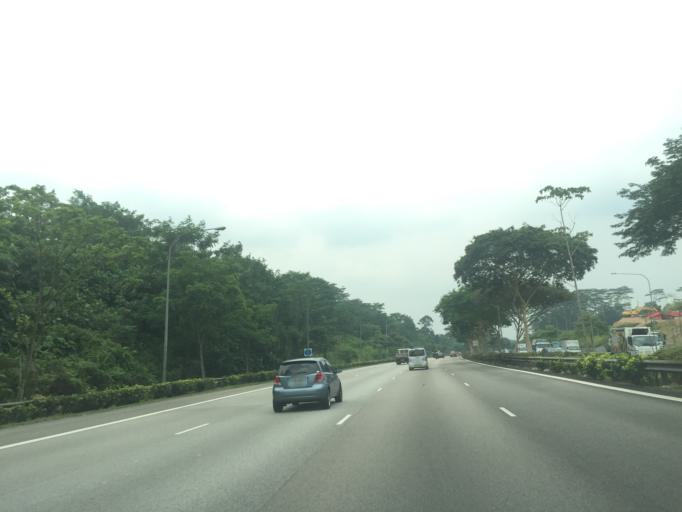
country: MY
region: Johor
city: Johor Bahru
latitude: 1.3897
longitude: 103.7604
